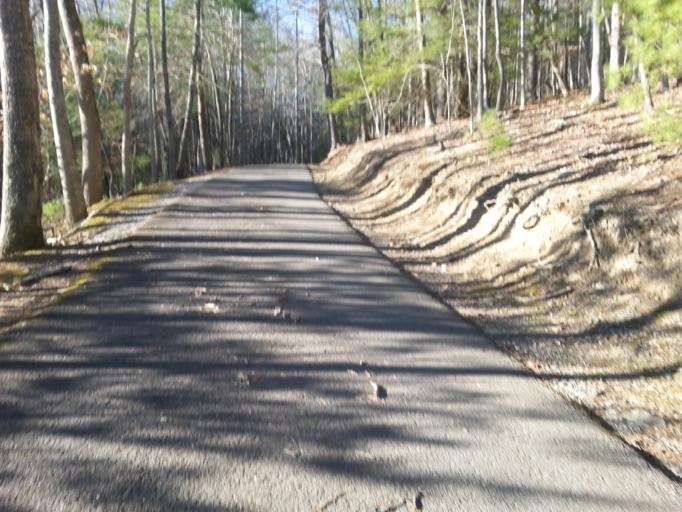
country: US
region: West Virginia
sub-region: Mercer County
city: Athens
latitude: 37.5375
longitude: -80.9819
